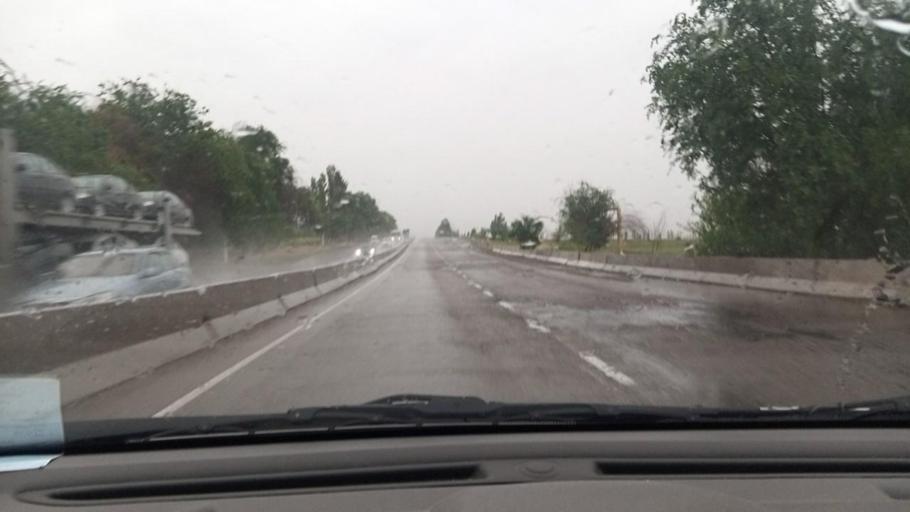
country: UZ
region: Toshkent
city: Angren
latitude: 40.9650
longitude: 69.9558
